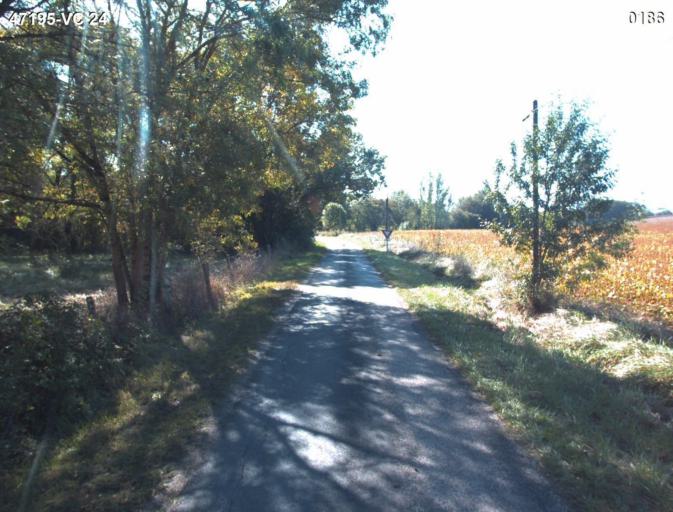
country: FR
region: Aquitaine
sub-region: Departement du Lot-et-Garonne
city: Nerac
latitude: 44.1634
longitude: 0.3646
